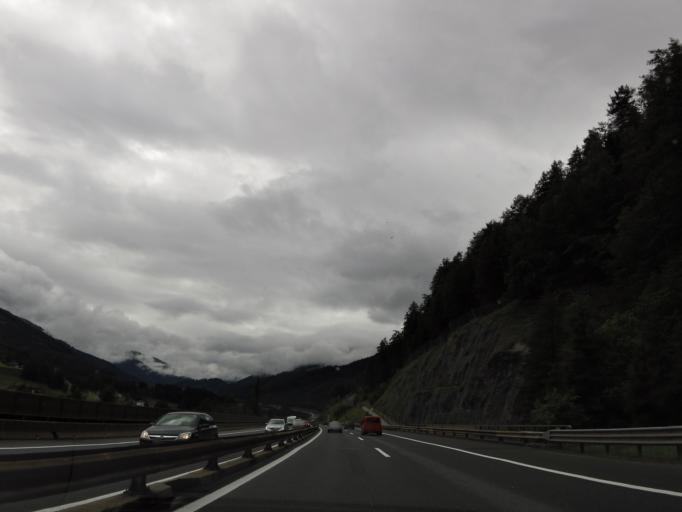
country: AT
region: Tyrol
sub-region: Politischer Bezirk Innsbruck Land
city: Matrei am Brenner
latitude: 47.1310
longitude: 11.4498
